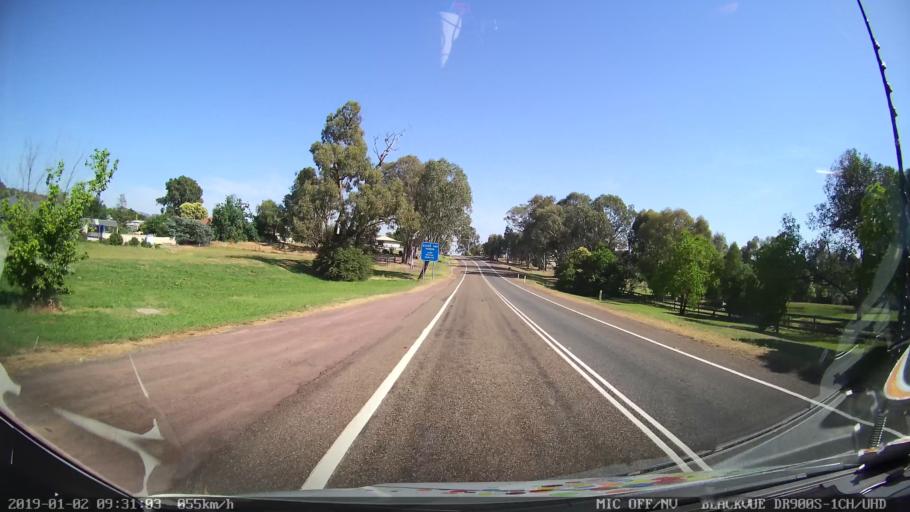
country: AU
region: New South Wales
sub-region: Tumut Shire
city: Tumut
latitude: -35.3215
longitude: 148.2371
